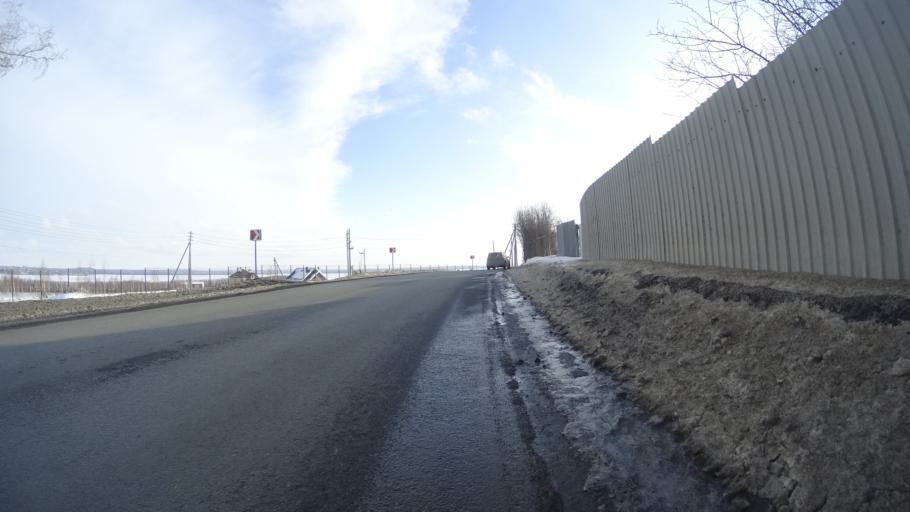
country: RU
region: Chelyabinsk
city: Sargazy
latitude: 55.1250
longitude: 61.2896
